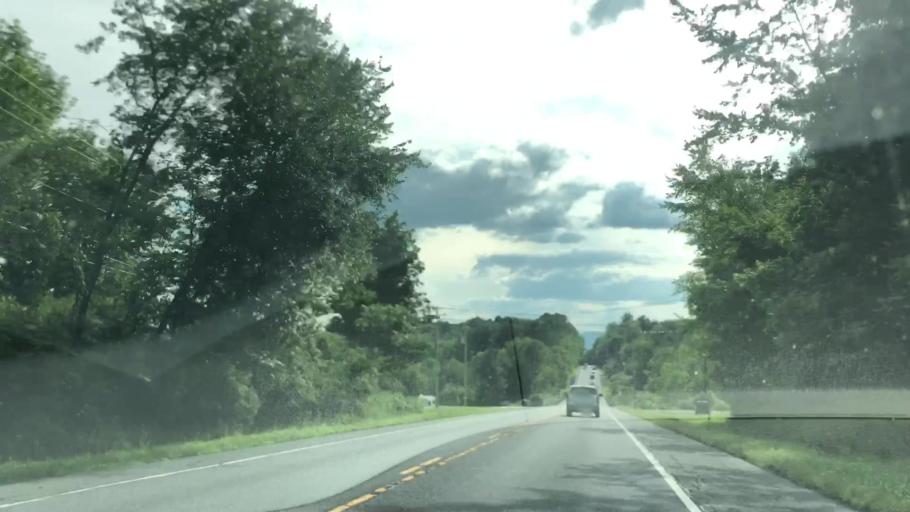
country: US
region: Vermont
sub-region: Rutland County
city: Fair Haven
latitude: 43.5682
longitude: -73.3225
